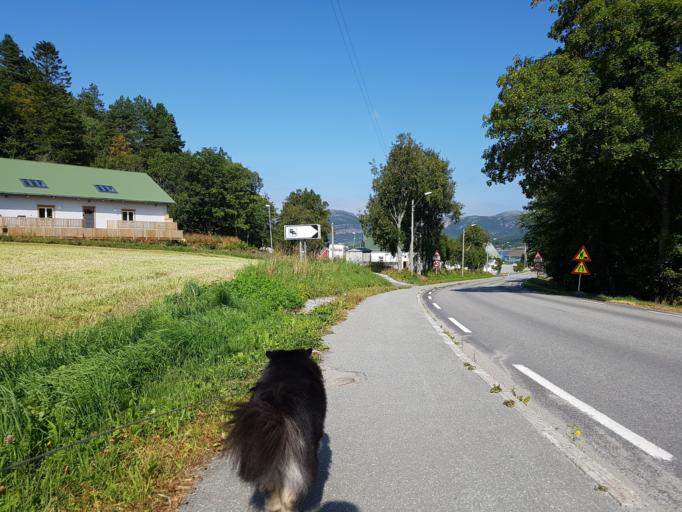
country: NO
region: Sor-Trondelag
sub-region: Agdenes
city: Lensvik
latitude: 63.6301
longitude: 9.8248
